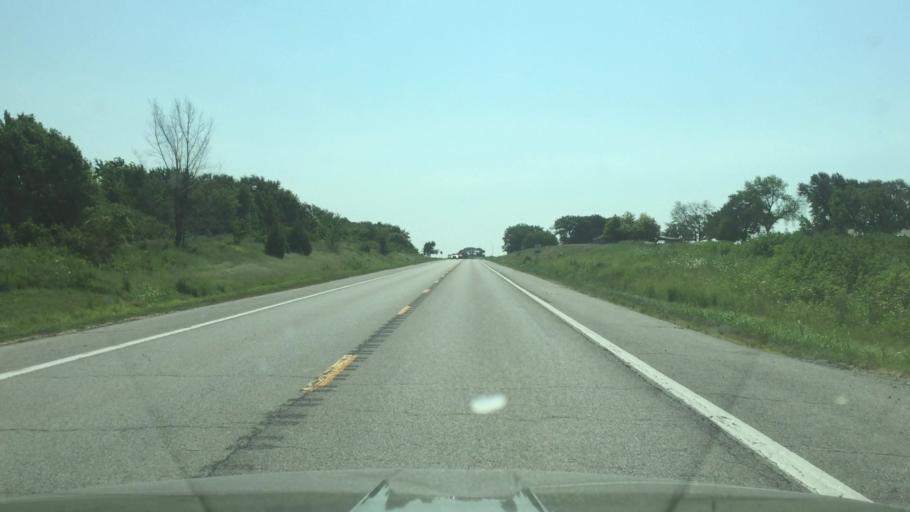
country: US
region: Missouri
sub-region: Pettis County
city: Sedalia
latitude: 38.6923
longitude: -93.0694
